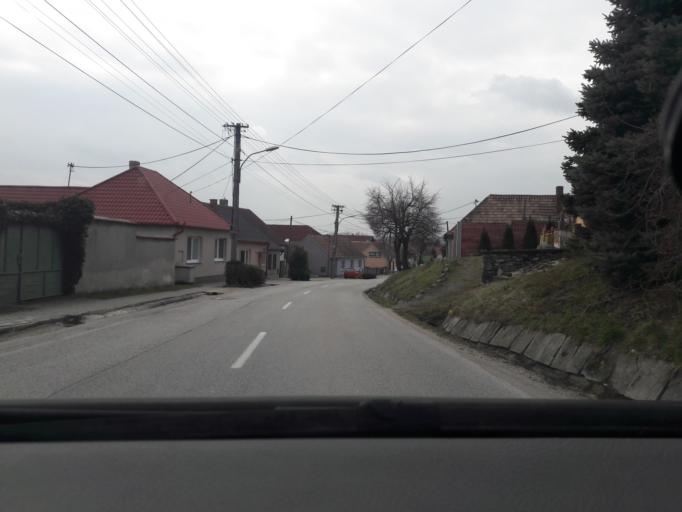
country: SK
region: Trnavsky
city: Smolenice
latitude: 48.4623
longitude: 17.4362
